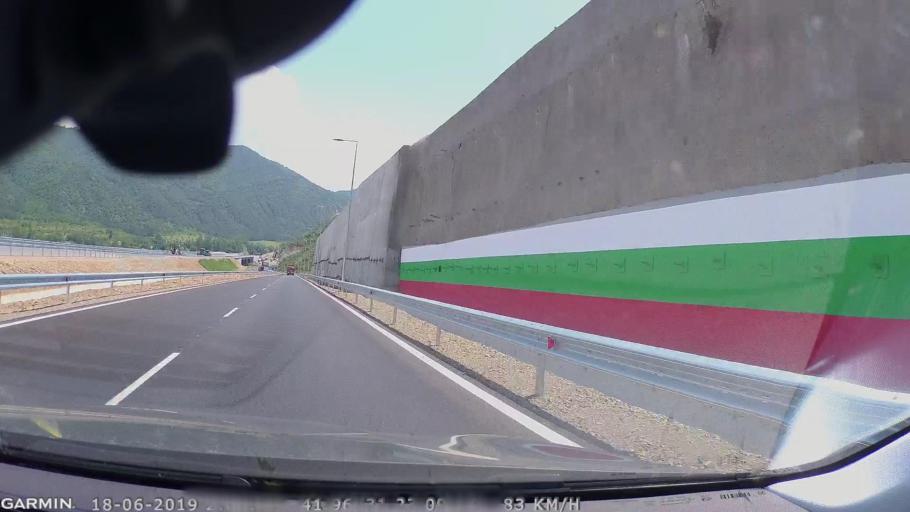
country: BG
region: Blagoevgrad
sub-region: Obshtina Blagoevgrad
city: Blagoevgrad
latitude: 41.9648
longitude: 23.0949
